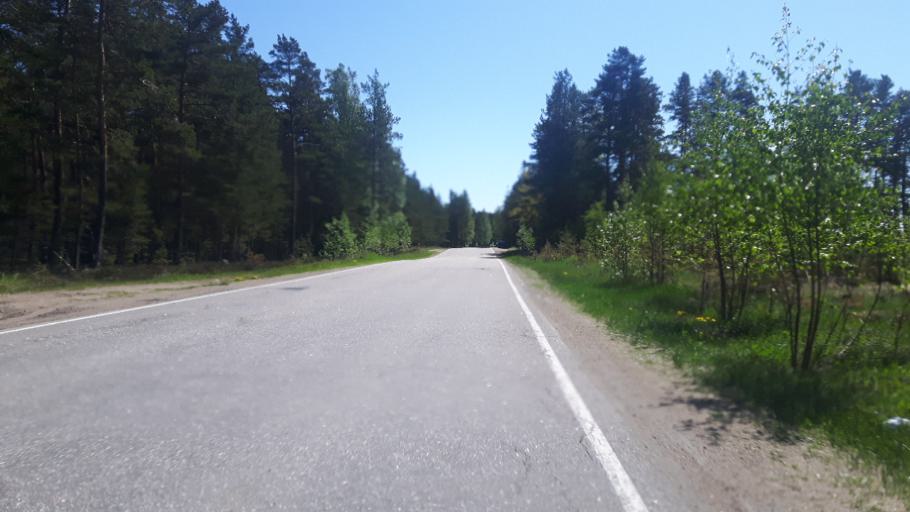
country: RU
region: Leningrad
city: Glebychevo
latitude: 60.3330
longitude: 28.8208
